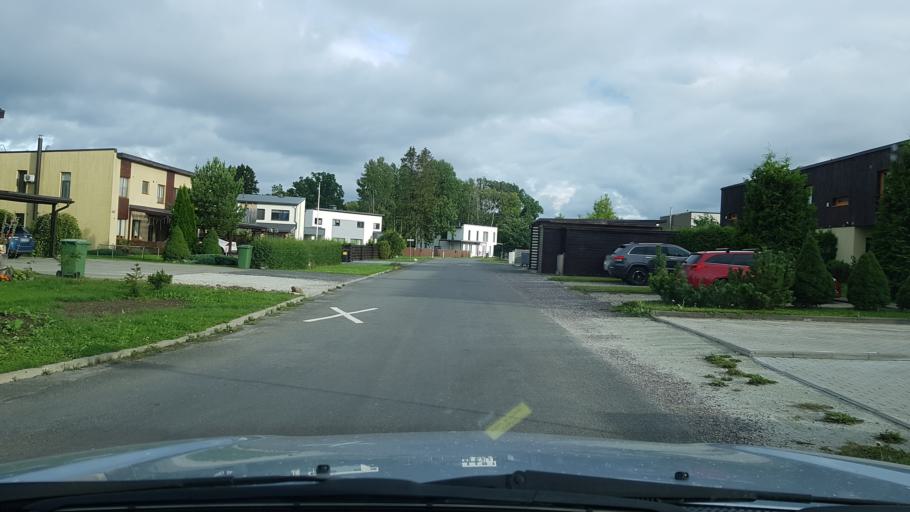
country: EE
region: Harju
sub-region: Rae vald
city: Jueri
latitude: 59.3647
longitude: 24.9196
